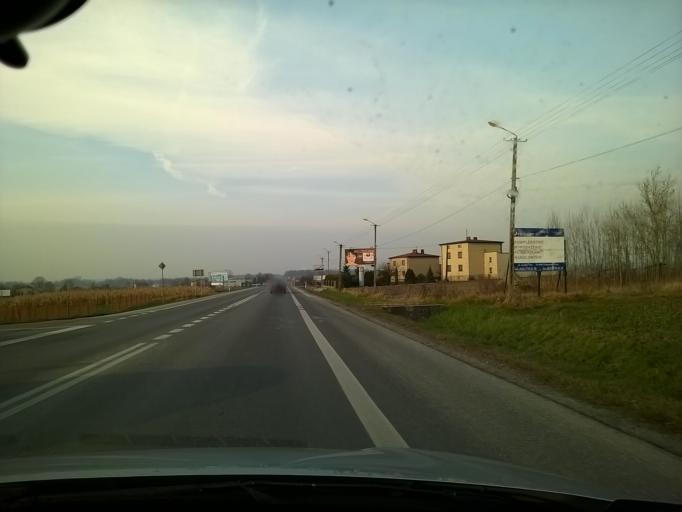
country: PL
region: Silesian Voivodeship
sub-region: Powiat gliwicki
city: Paniowki
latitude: 50.2358
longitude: 18.7812
